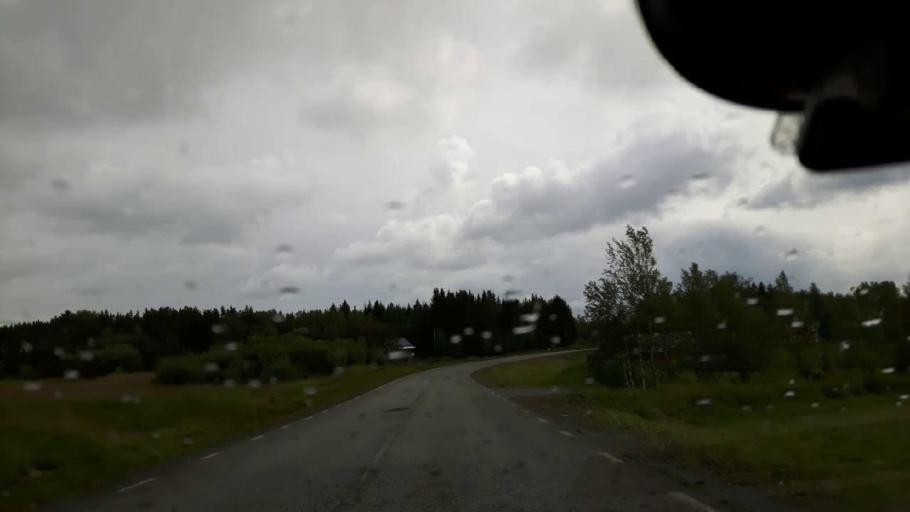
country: SE
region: Jaemtland
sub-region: Krokoms Kommun
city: Valla
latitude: 63.4196
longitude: 13.7924
